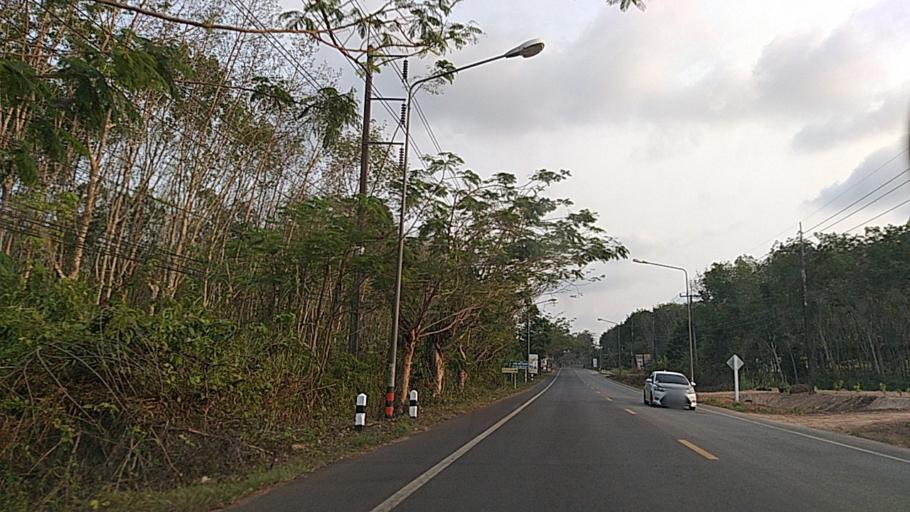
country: TH
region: Trat
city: Laem Ngop
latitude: 12.2732
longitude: 102.3057
